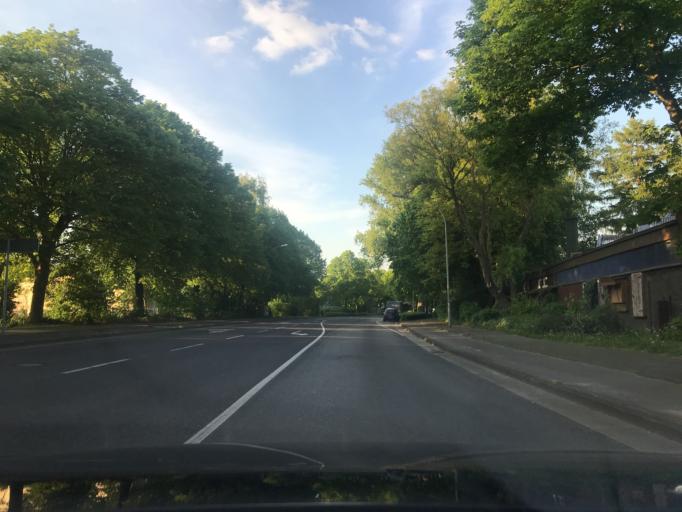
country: DE
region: North Rhine-Westphalia
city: Wegberg
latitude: 51.1461
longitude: 6.3546
